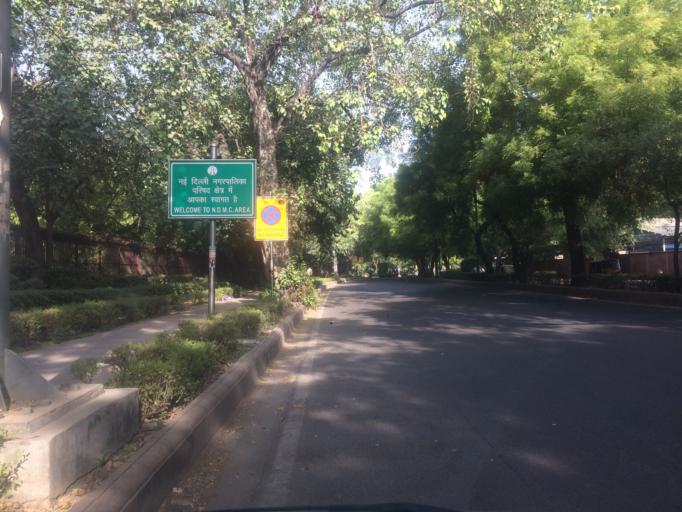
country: IN
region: NCT
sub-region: New Delhi
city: New Delhi
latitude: 28.6092
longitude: 77.2393
